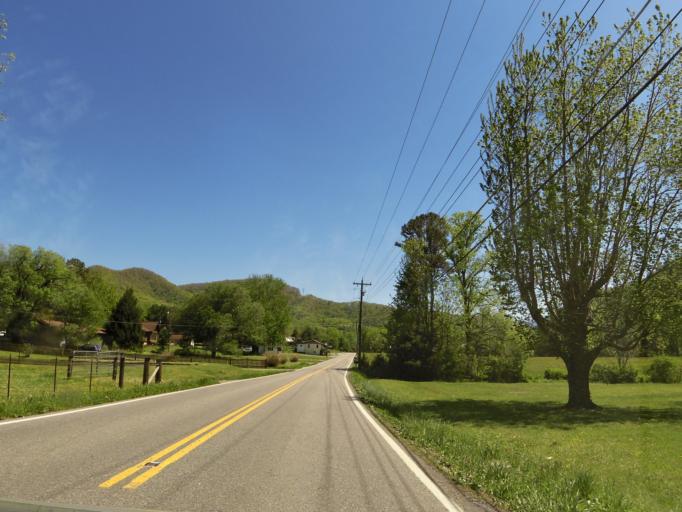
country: US
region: Tennessee
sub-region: Unicoi County
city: Erwin
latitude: 36.1755
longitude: -82.4506
